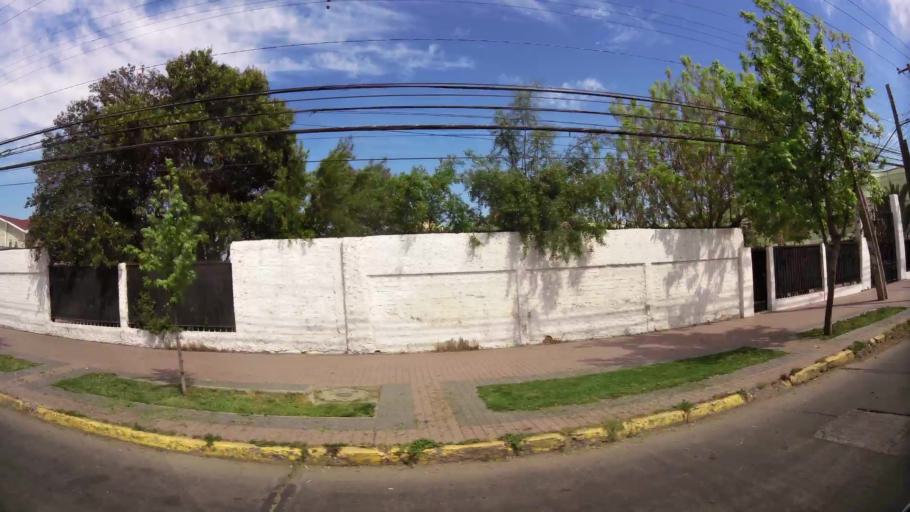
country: CL
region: Santiago Metropolitan
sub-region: Provincia de Talagante
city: Talagante
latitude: -33.6649
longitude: -70.9233
